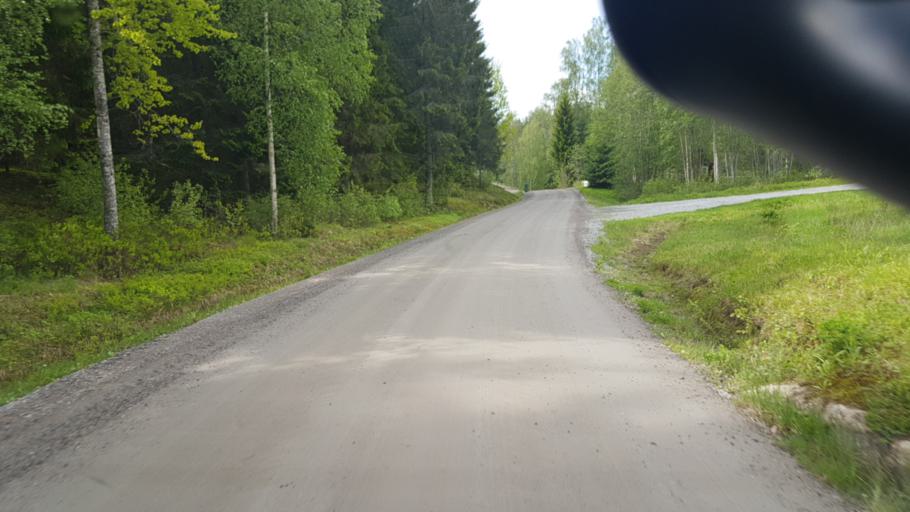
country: NO
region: Ostfold
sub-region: Romskog
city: Romskog
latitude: 59.6898
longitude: 11.9391
